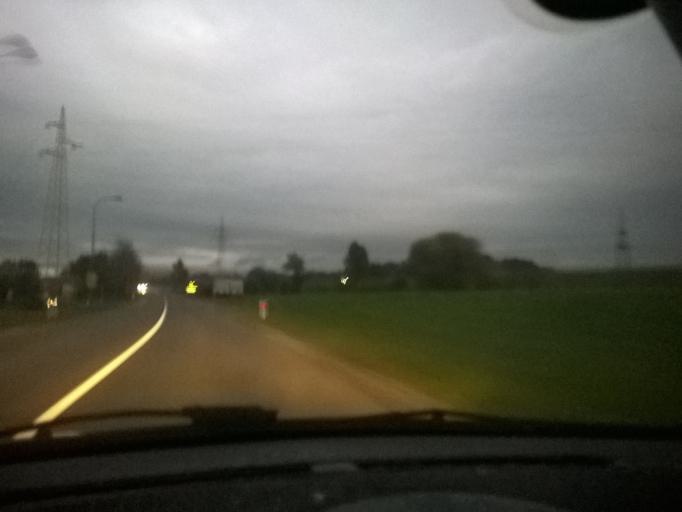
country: HR
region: Krapinsko-Zagorska
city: Zabok
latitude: 46.0238
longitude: 15.9099
